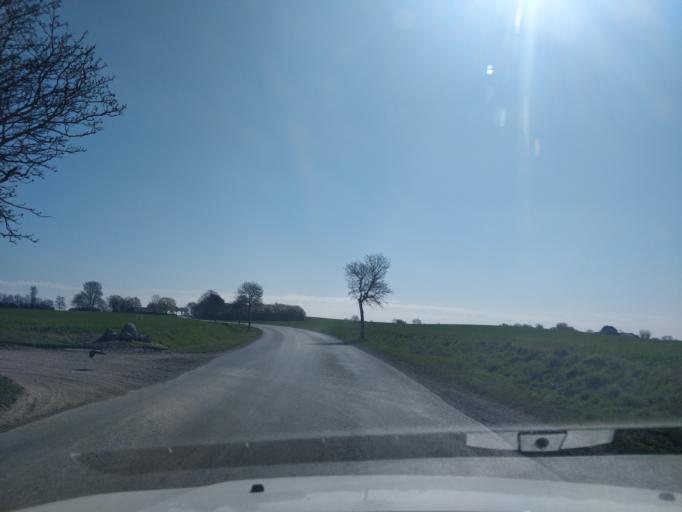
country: DK
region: Zealand
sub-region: Vordingborg Kommune
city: Stege
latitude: 54.9863
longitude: 12.3874
